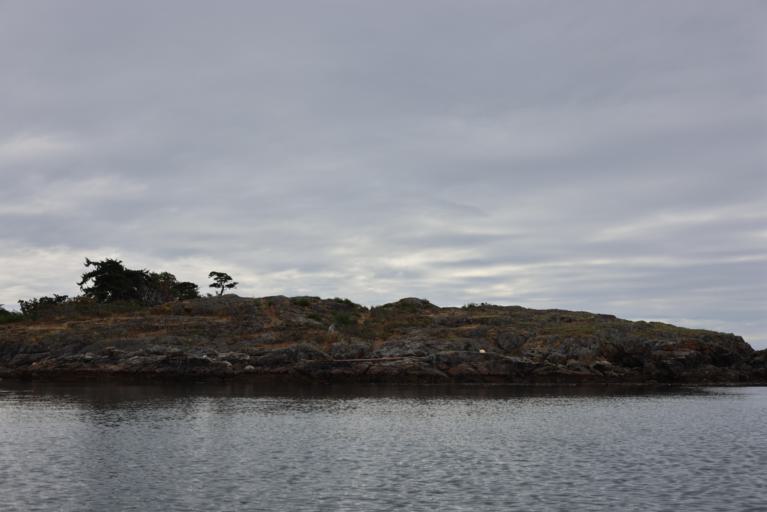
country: CA
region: British Columbia
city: Oak Bay
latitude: 48.4489
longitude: -123.2810
